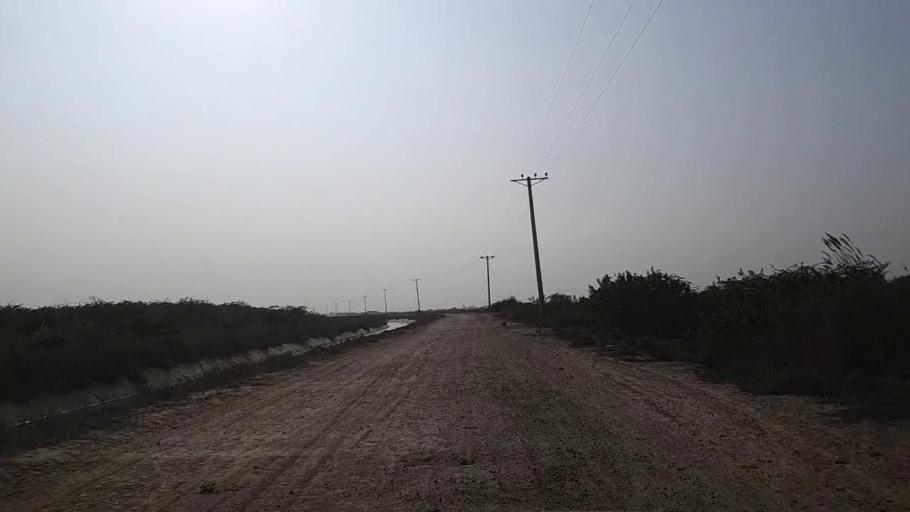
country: PK
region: Sindh
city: Keti Bandar
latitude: 24.1962
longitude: 67.6159
